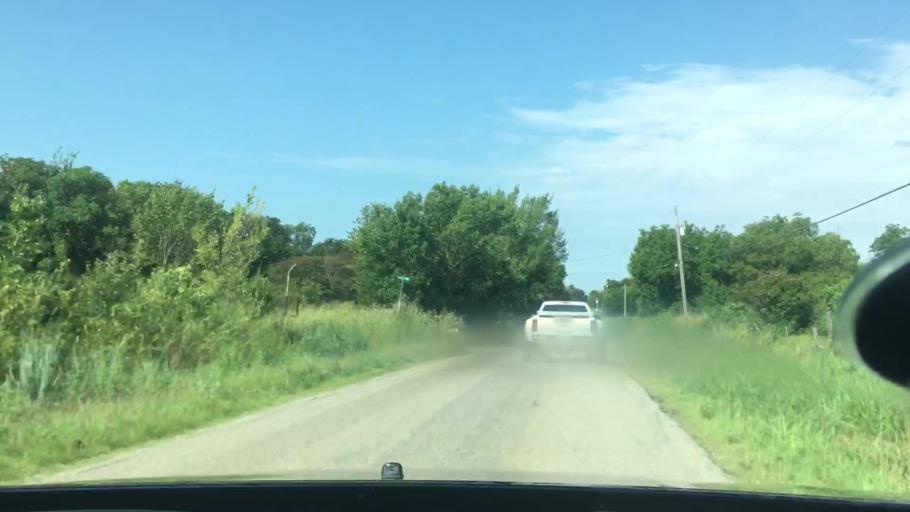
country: US
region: Oklahoma
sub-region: Bryan County
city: Colbert
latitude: 33.9110
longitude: -96.5284
